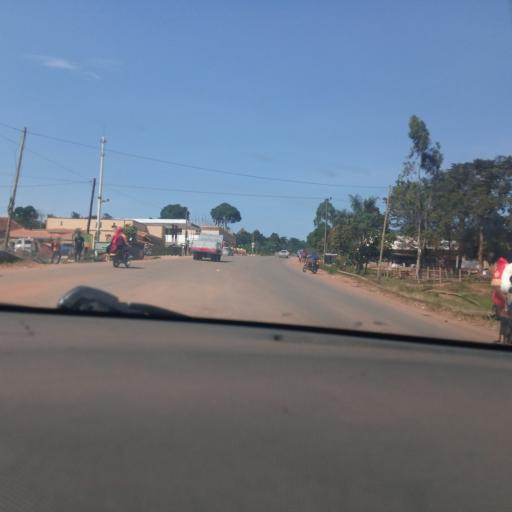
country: UG
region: Central Region
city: Masaka
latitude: -0.3088
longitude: 31.7560
